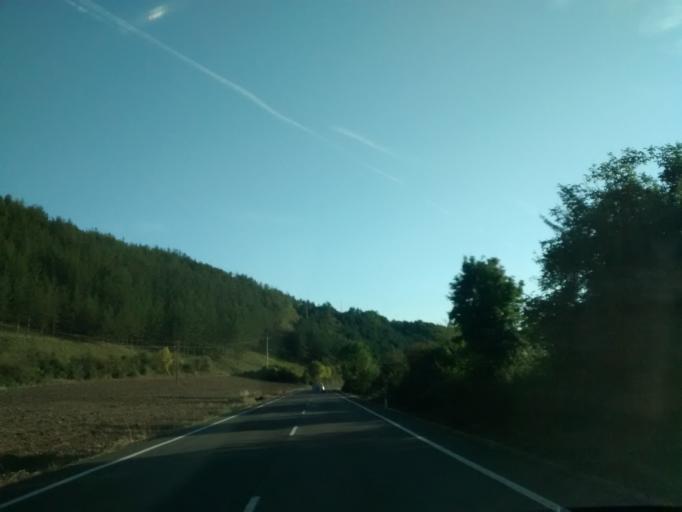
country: ES
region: Aragon
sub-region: Provincia de Huesca
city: Jasa
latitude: 42.6121
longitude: -0.7237
